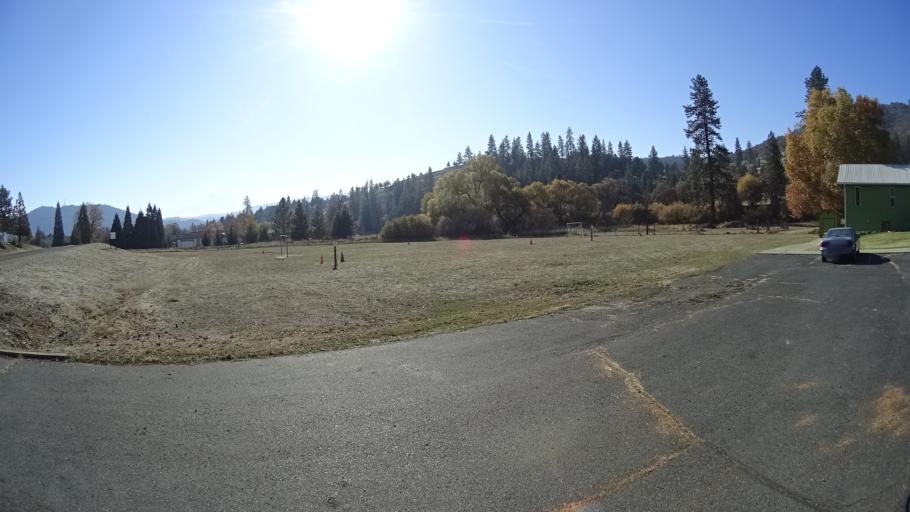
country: US
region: California
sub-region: Siskiyou County
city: Yreka
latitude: 41.7324
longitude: -122.6555
